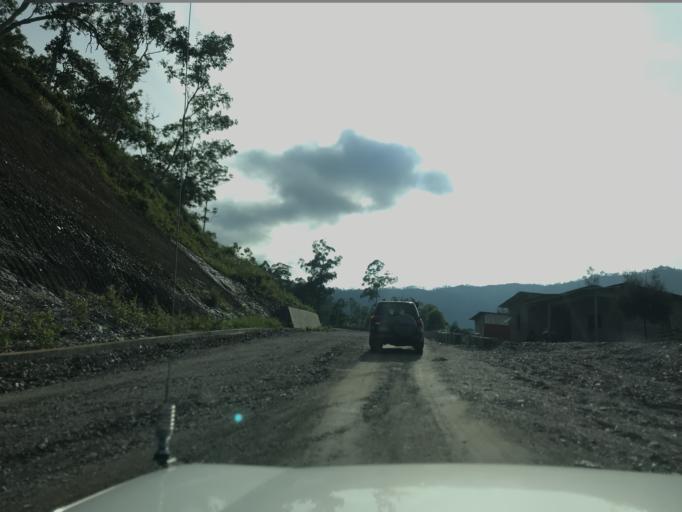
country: TL
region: Aileu
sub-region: Aileu Villa
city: Aileu
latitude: -8.6645
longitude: 125.5381
